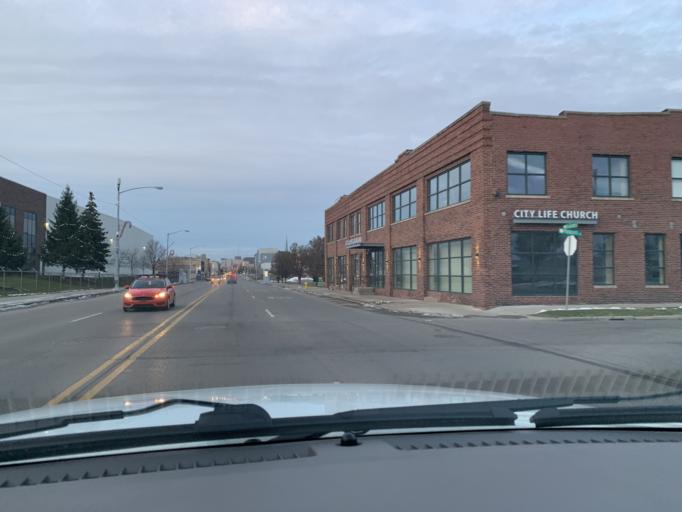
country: US
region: Michigan
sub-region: Kent County
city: Grand Rapids
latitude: 42.9516
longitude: -85.6675
